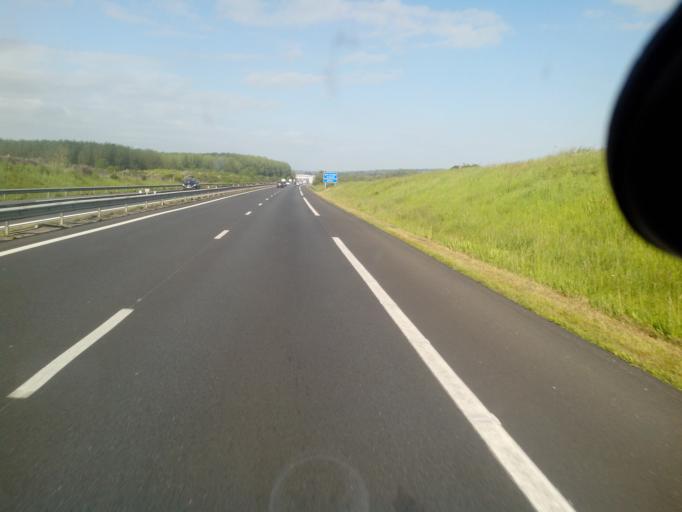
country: FR
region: Lower Normandy
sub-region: Departement du Calvados
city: Dives-sur-Mer
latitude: 49.2232
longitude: -0.1046
